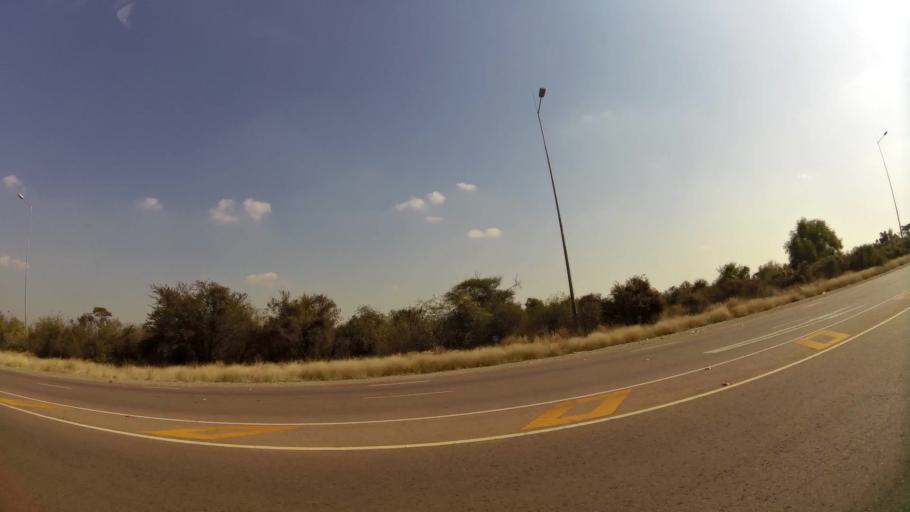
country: ZA
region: North-West
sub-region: Bojanala Platinum District Municipality
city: Mogwase
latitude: -25.4215
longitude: 27.0794
